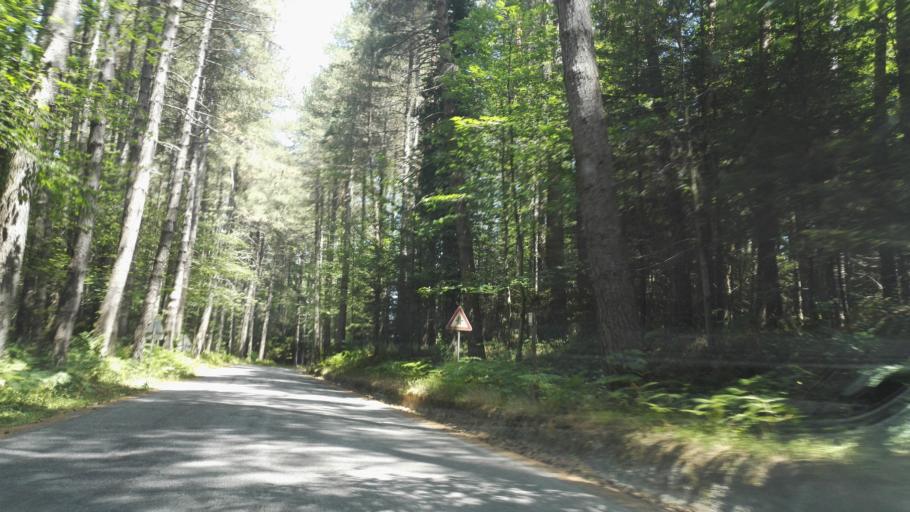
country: IT
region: Calabria
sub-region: Provincia di Vibo-Valentia
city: Mongiana
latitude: 38.5217
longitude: 16.3192
